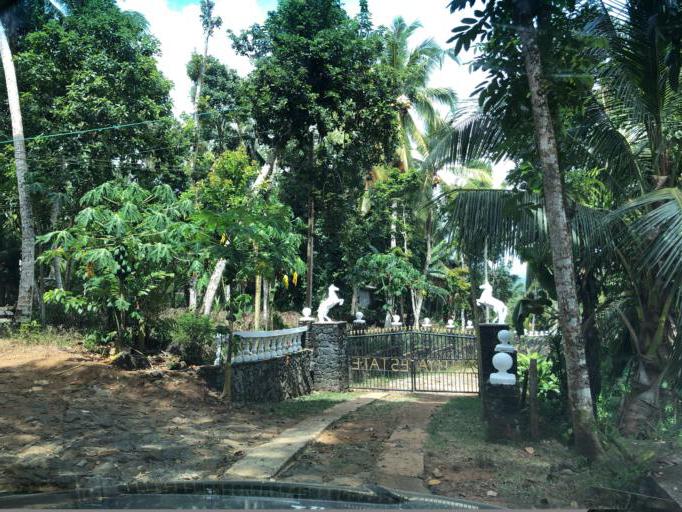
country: LK
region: Western
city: Horawala Junction
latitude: 6.5494
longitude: 80.0875
